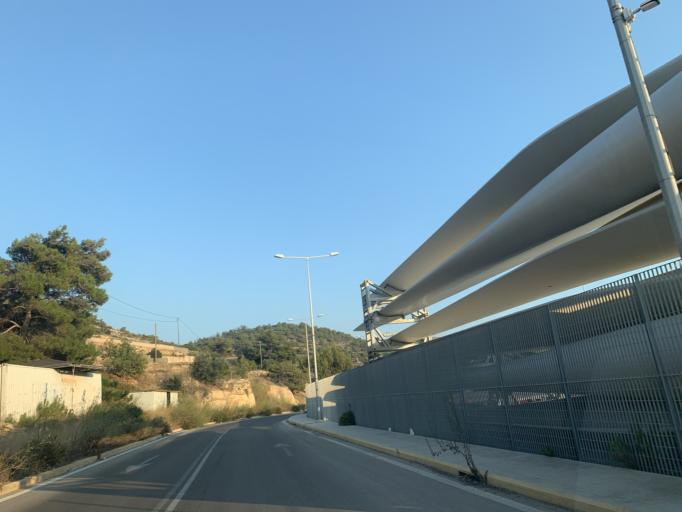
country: GR
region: North Aegean
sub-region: Chios
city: Thymiana
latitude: 38.2909
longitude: 25.9301
